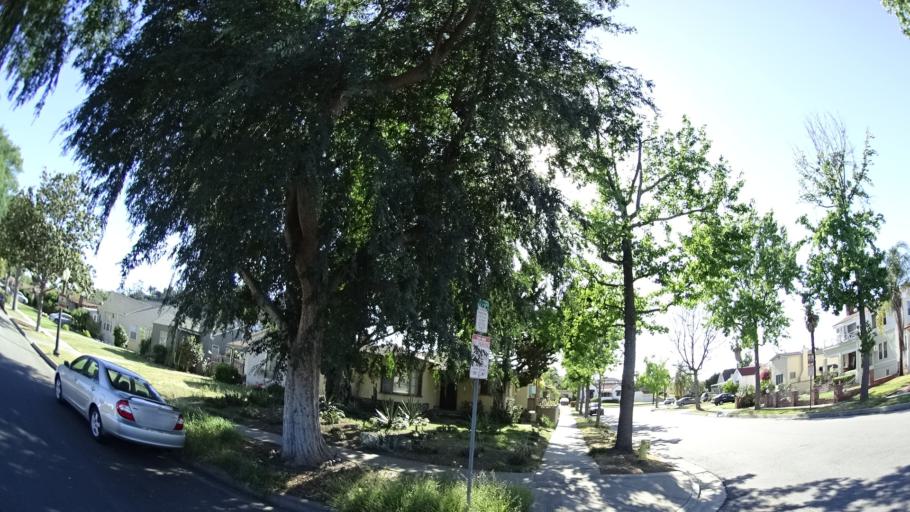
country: US
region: California
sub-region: Los Angeles County
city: Alhambra
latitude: 34.0756
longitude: -118.1530
